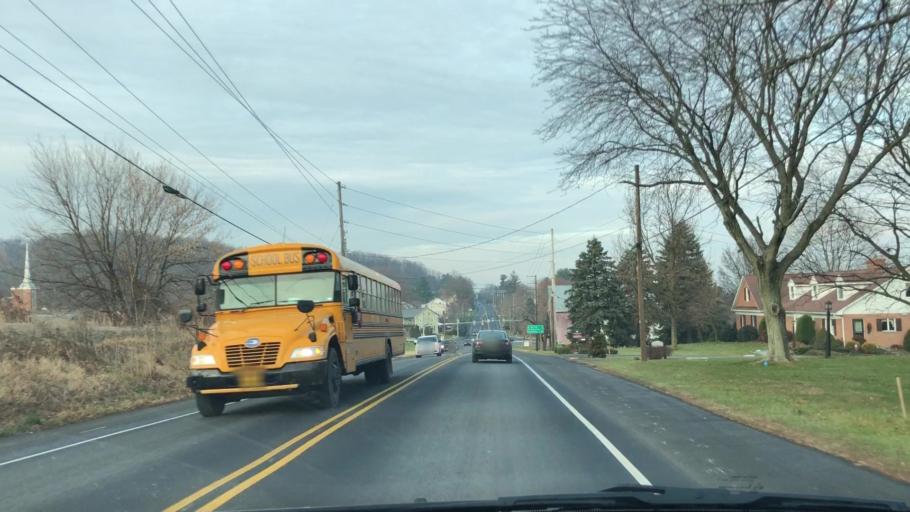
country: US
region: Pennsylvania
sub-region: Lancaster County
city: Mountville
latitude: 40.0579
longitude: -76.4007
